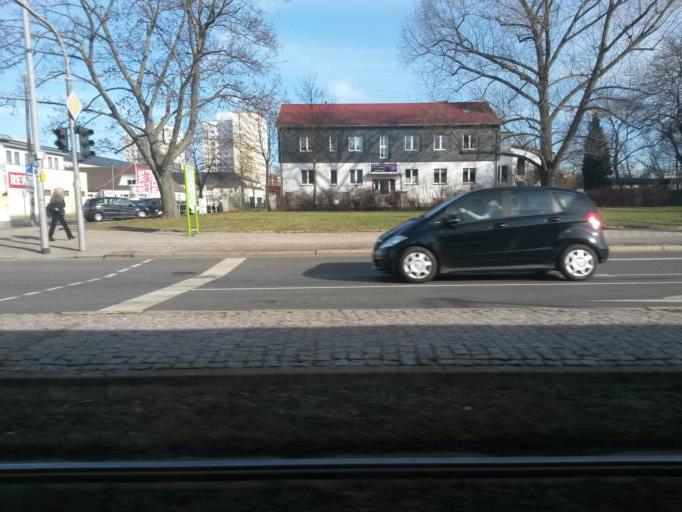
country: DE
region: Thuringia
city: Erfurt
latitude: 50.9913
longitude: 11.0261
